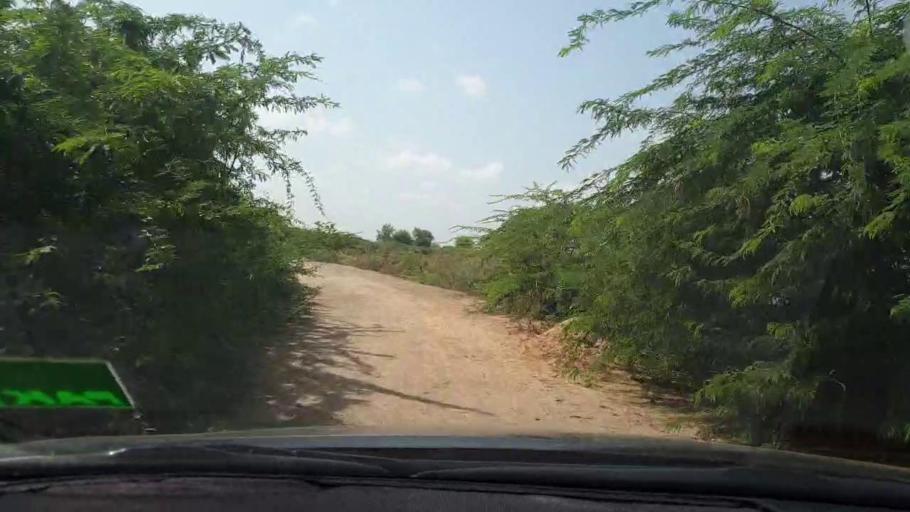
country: PK
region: Sindh
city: Tando Bago
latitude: 24.9358
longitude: 69.0464
